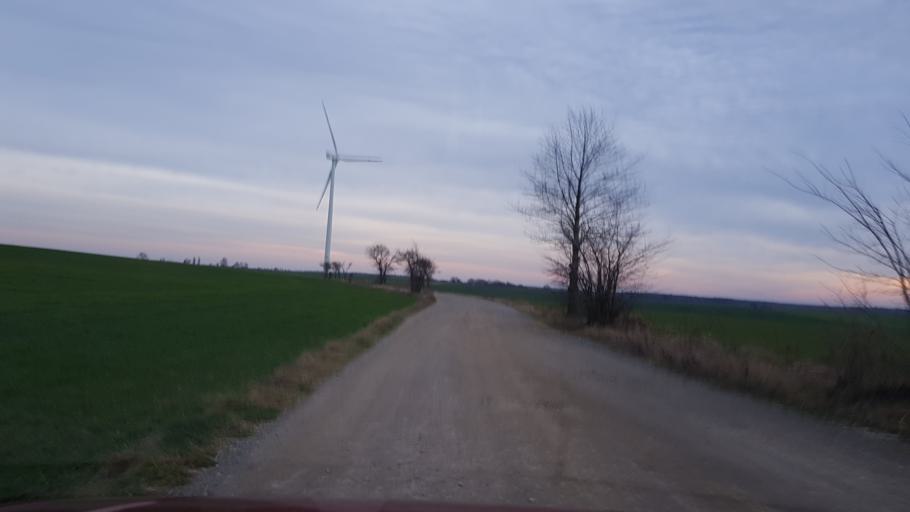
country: PL
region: West Pomeranian Voivodeship
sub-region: Powiat choszczenski
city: Pelczyce
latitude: 53.0399
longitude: 15.2562
